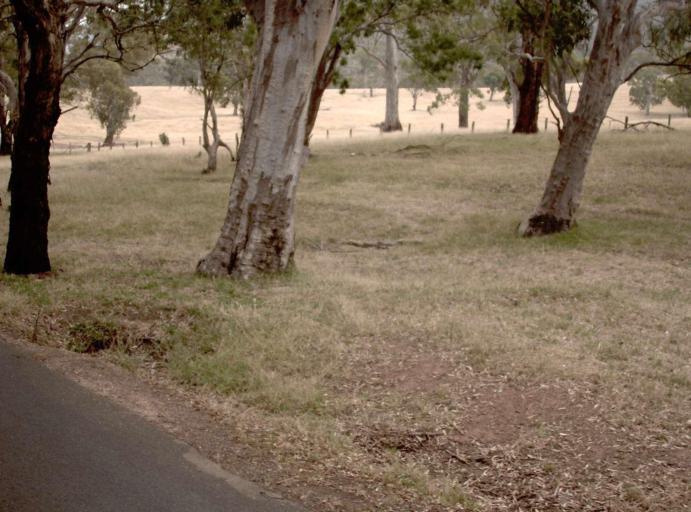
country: AU
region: Victoria
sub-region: Wellington
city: Heyfield
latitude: -37.6551
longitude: 146.6424
